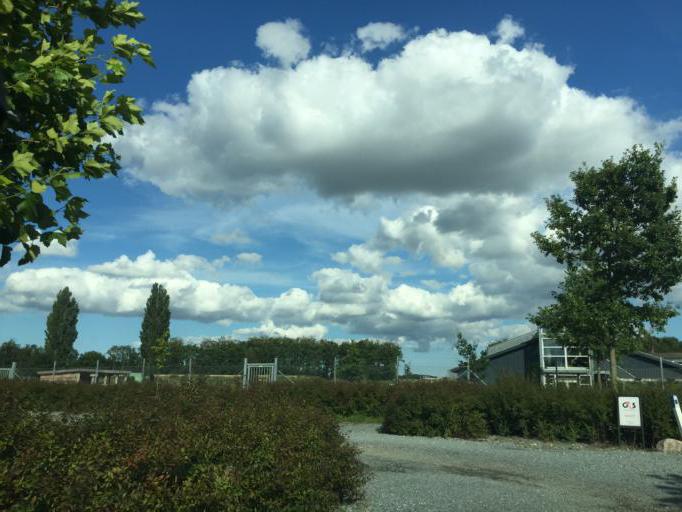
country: DK
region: South Denmark
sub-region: Odense Kommune
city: Odense
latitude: 55.3651
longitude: 10.4076
